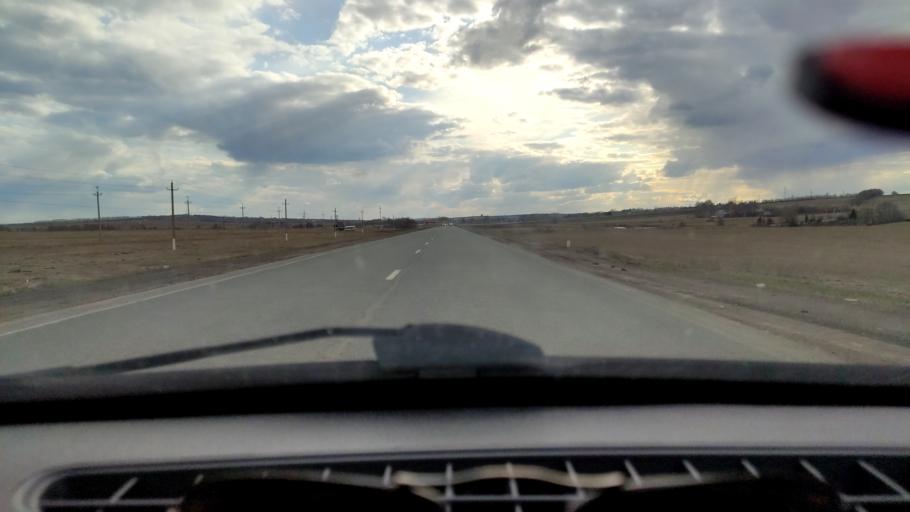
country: RU
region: Bashkortostan
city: Karmaskaly
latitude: 54.3869
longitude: 56.2314
